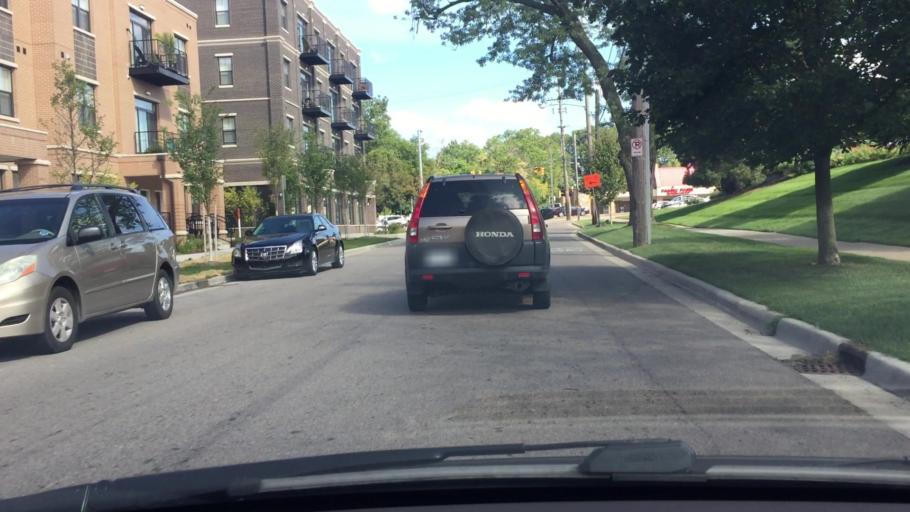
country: US
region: Michigan
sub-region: Kent County
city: Grand Rapids
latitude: 42.9619
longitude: -85.6359
